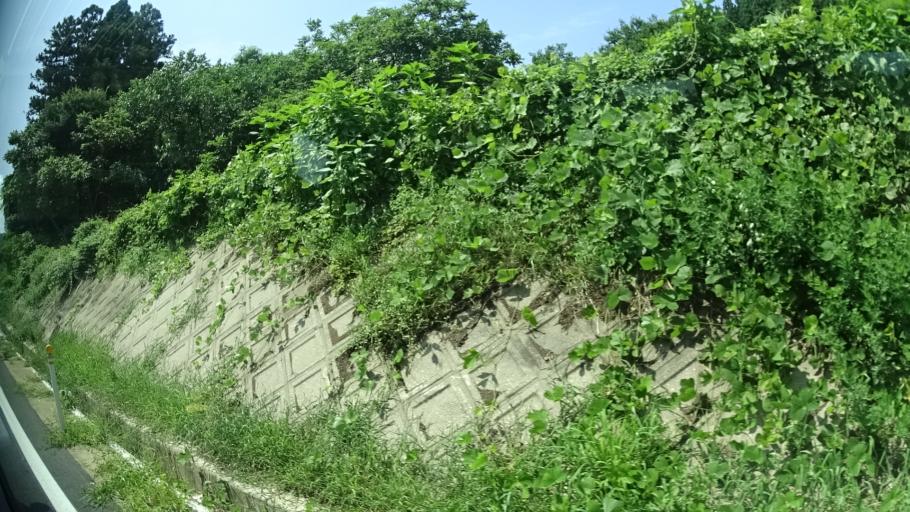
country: JP
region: Miyagi
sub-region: Oshika Gun
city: Onagawa Cho
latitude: 38.6459
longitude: 141.4147
